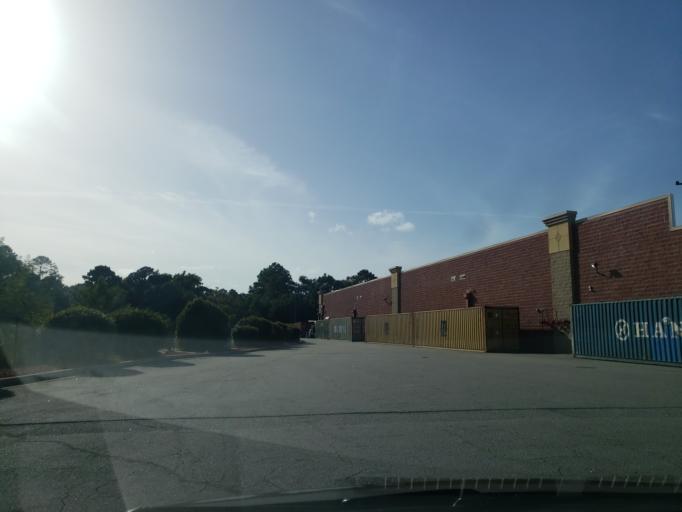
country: US
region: Georgia
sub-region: Chatham County
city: Isle of Hope
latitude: 31.9860
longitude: -81.0827
